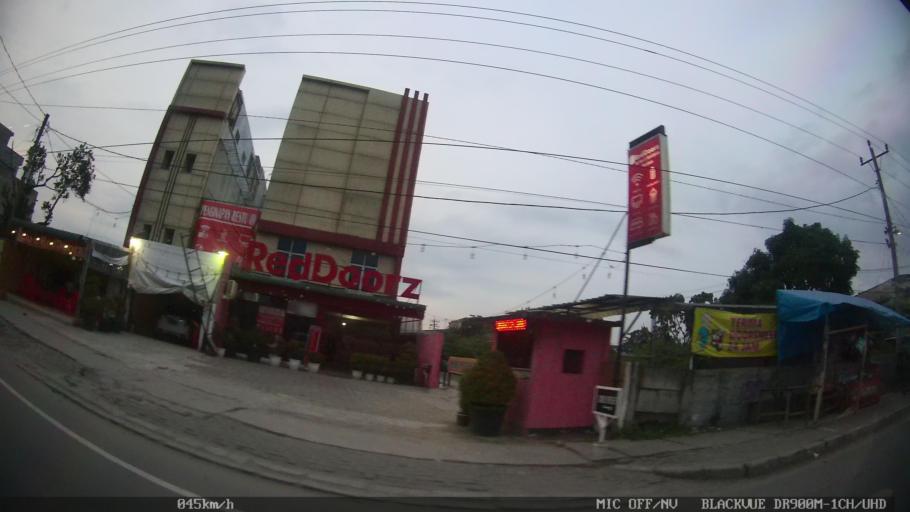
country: ID
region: North Sumatra
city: Sunggal
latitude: 3.5974
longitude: 98.6112
